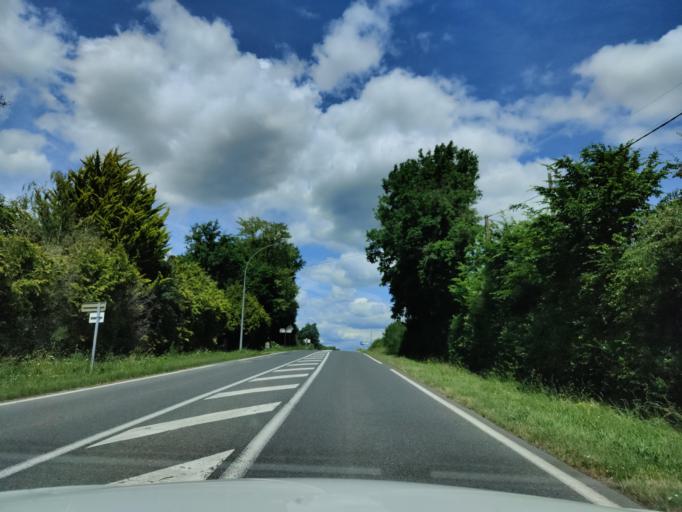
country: FR
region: Centre
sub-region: Departement du Cher
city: Henrichemont
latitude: 47.3682
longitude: 2.4325
